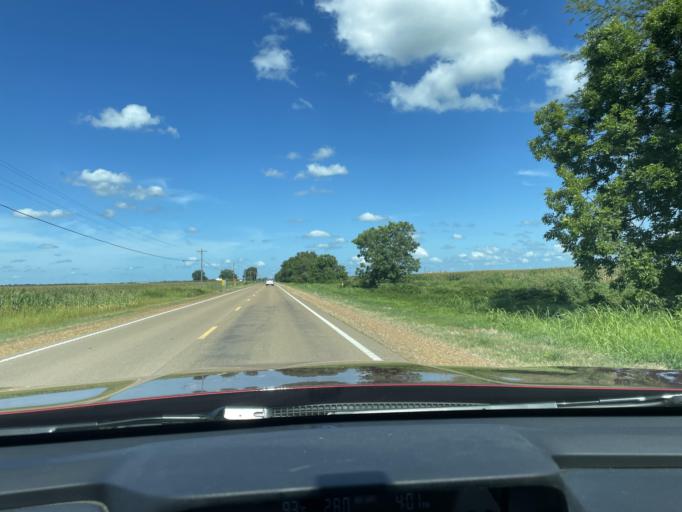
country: US
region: Mississippi
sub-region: Humphreys County
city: Belzoni
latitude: 33.1837
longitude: -90.5311
